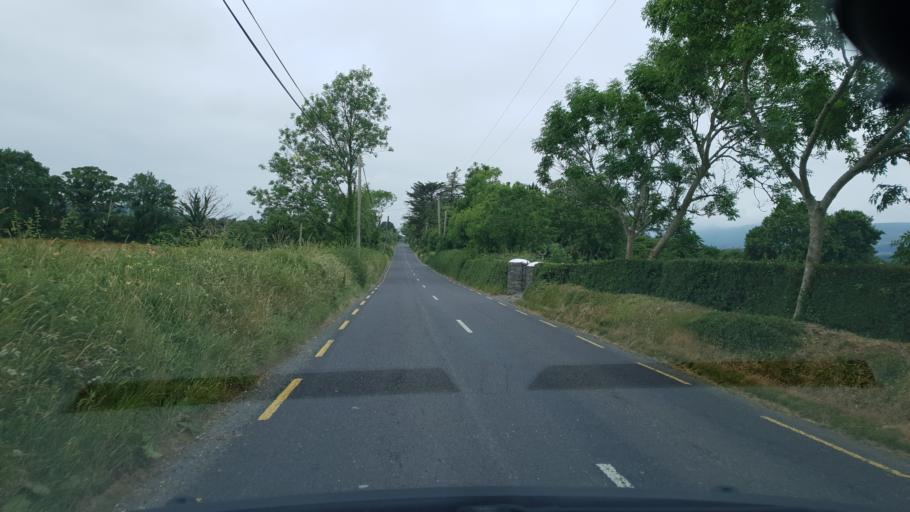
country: IE
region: Munster
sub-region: Ciarrai
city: Tralee
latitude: 52.1637
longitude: -9.6134
